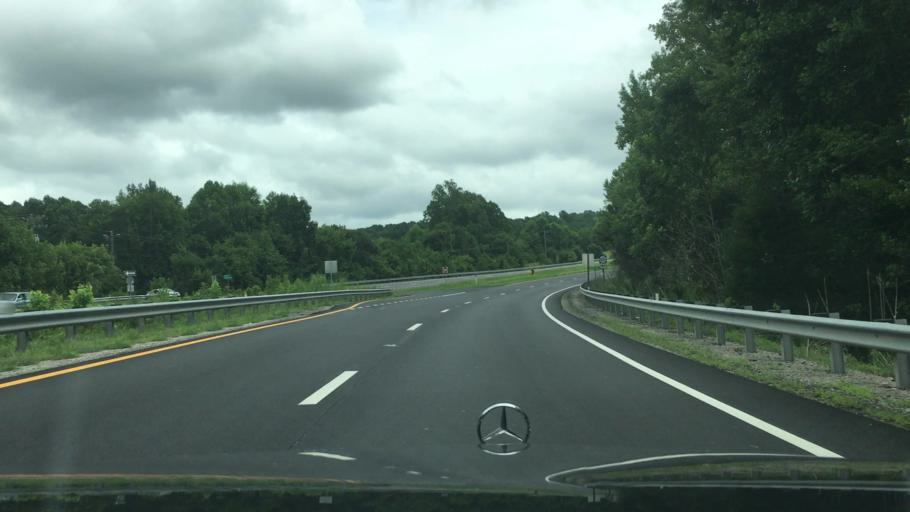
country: US
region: Virginia
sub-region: Prince Edward County
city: Farmville
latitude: 37.2756
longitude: -78.3203
